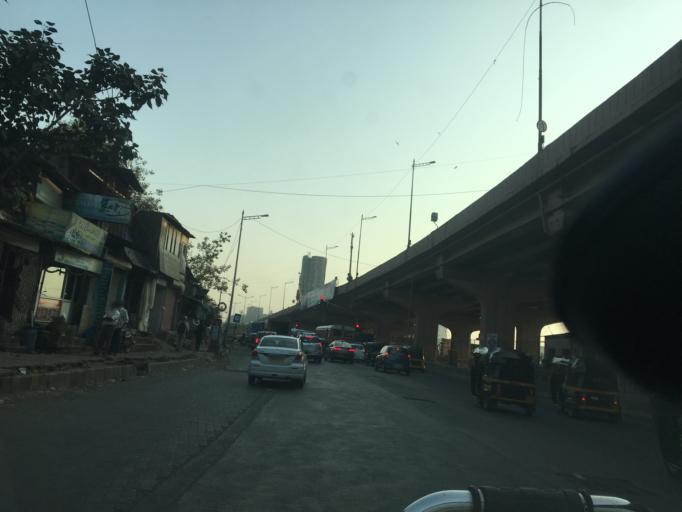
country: IN
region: Maharashtra
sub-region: Mumbai Suburban
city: Powai
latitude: 19.1416
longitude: 72.8551
